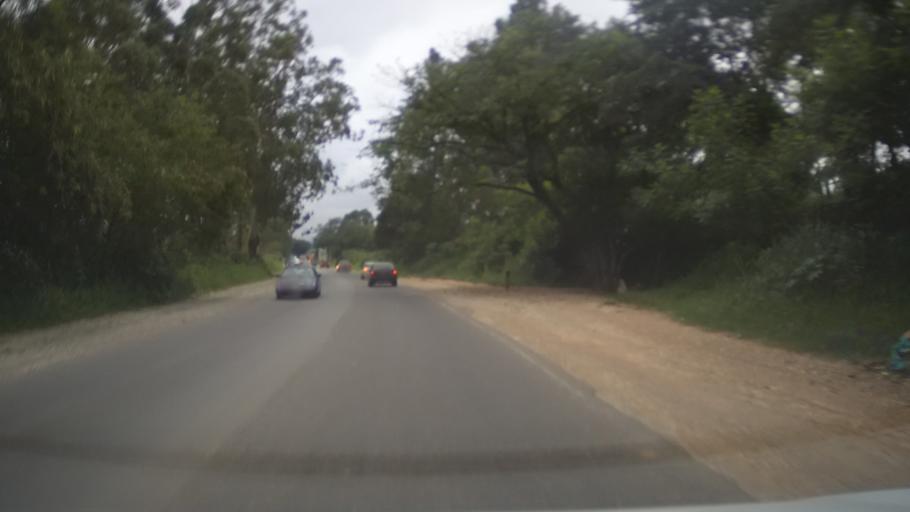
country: BR
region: Sao Paulo
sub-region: Guarulhos
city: Guarulhos
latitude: -23.3944
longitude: -46.4444
